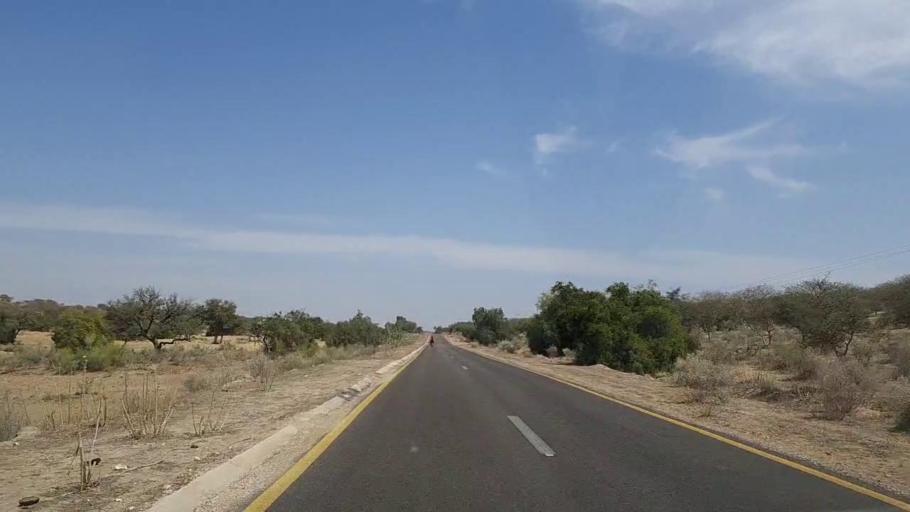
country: PK
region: Sindh
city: Mithi
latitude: 24.8770
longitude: 69.8616
